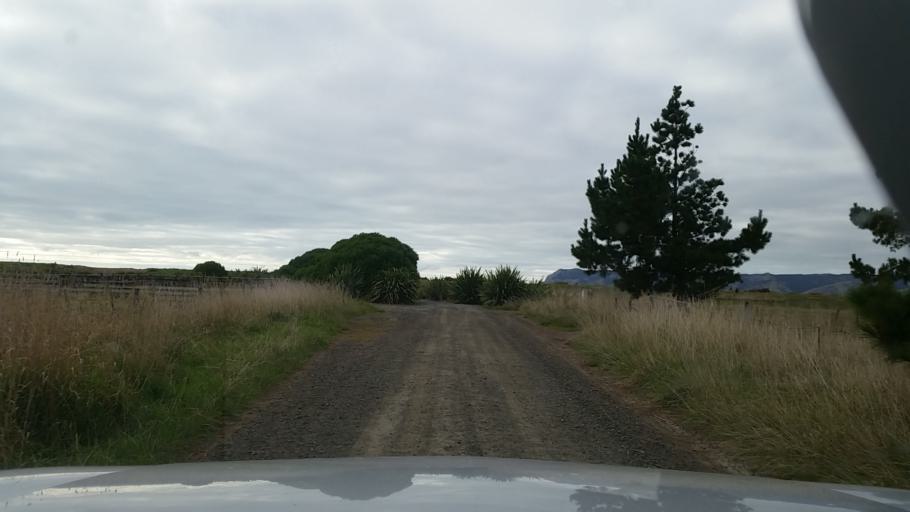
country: NZ
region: Marlborough
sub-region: Marlborough District
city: Blenheim
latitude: -41.5134
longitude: 174.0449
